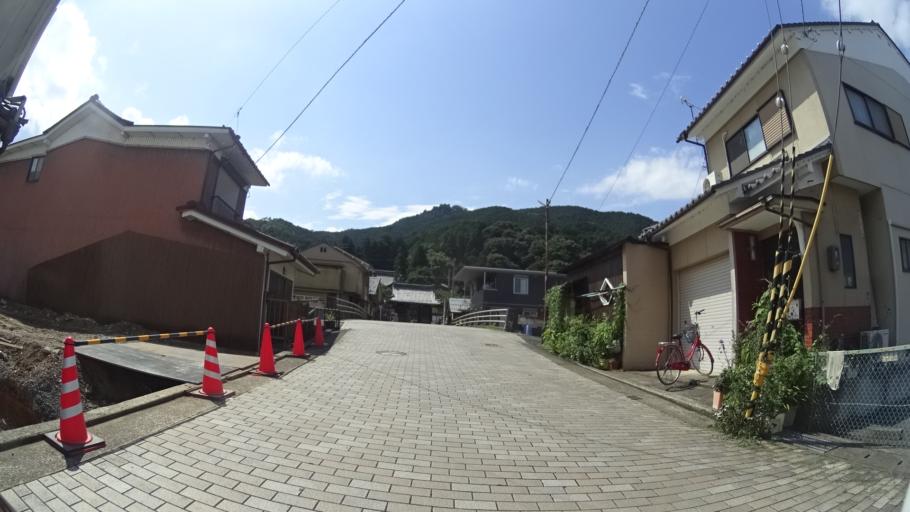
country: JP
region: Kyoto
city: Maizuru
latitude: 35.4432
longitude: 135.3257
